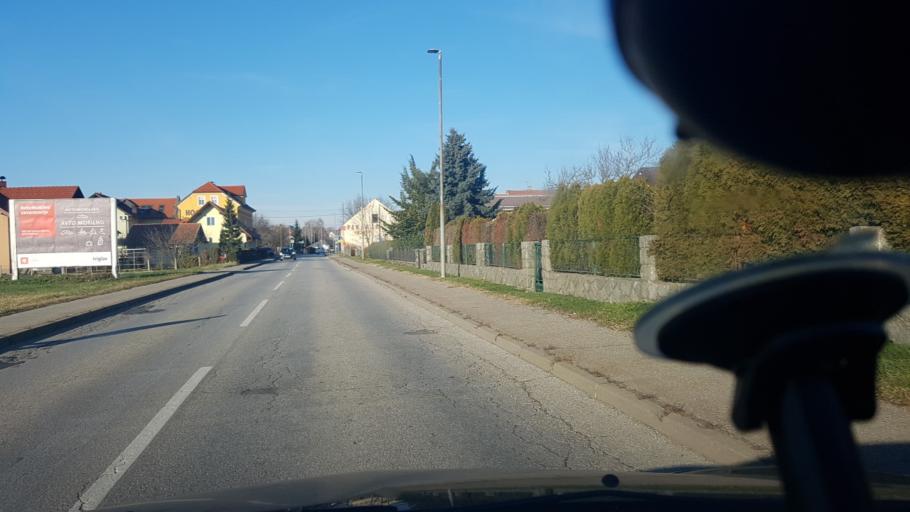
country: SI
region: Ptuj
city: Ptuj
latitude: 46.4129
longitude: 15.8648
